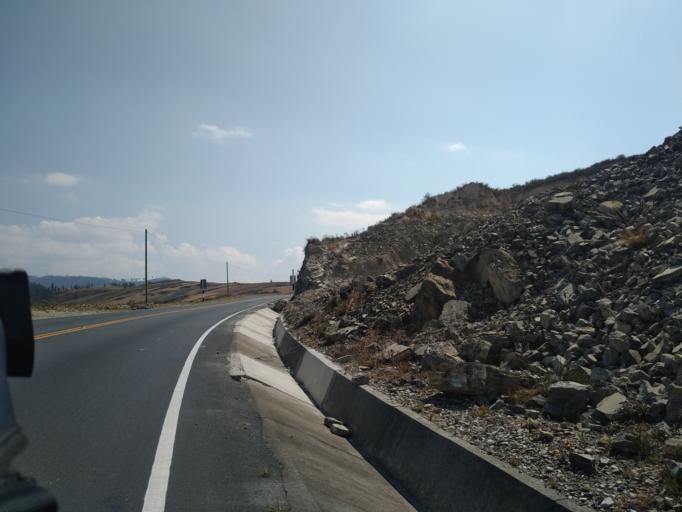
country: PE
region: Cajamarca
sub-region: Provincia de Cajamarca
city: Llacanora
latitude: -7.2077
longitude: -78.3935
